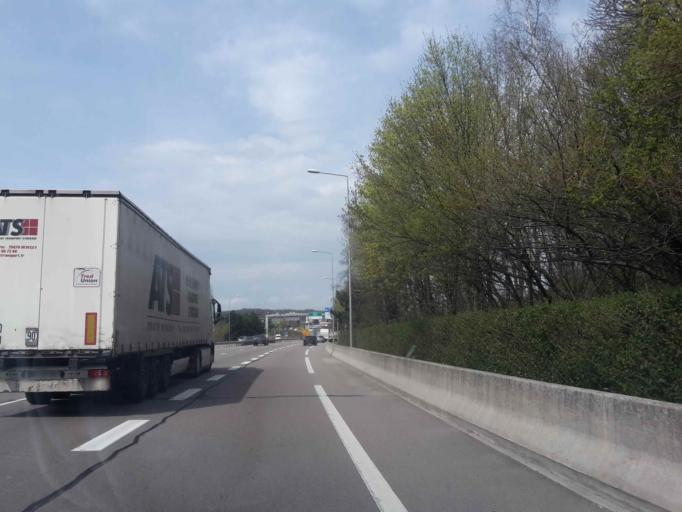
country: FR
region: Franche-Comte
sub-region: Departement du Doubs
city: Miserey-Salines
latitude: 47.2735
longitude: 5.9964
